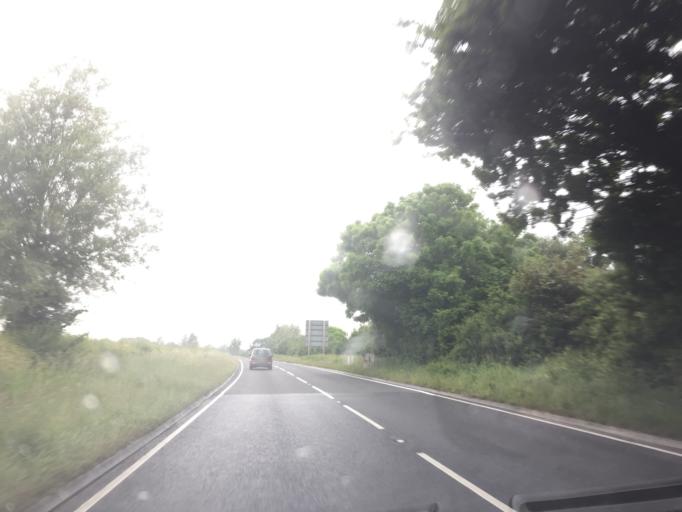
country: GB
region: England
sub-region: Dorset
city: Lytchett Matravers
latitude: 50.7330
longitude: -2.0684
